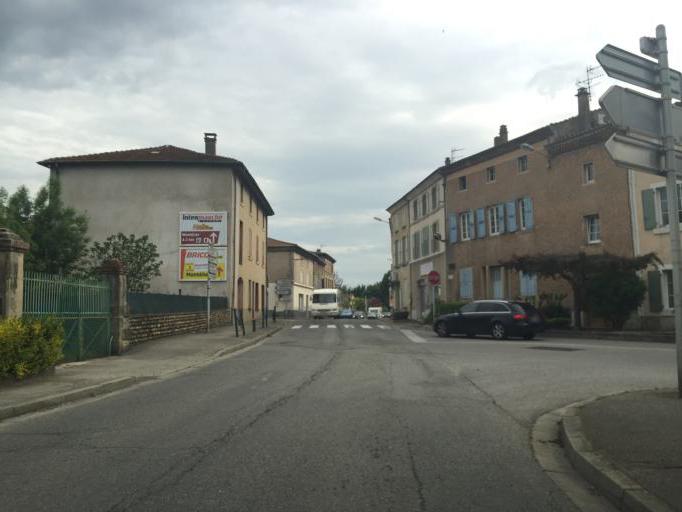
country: FR
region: Rhone-Alpes
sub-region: Departement de la Drome
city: Alixan
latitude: 44.9754
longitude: 5.0278
